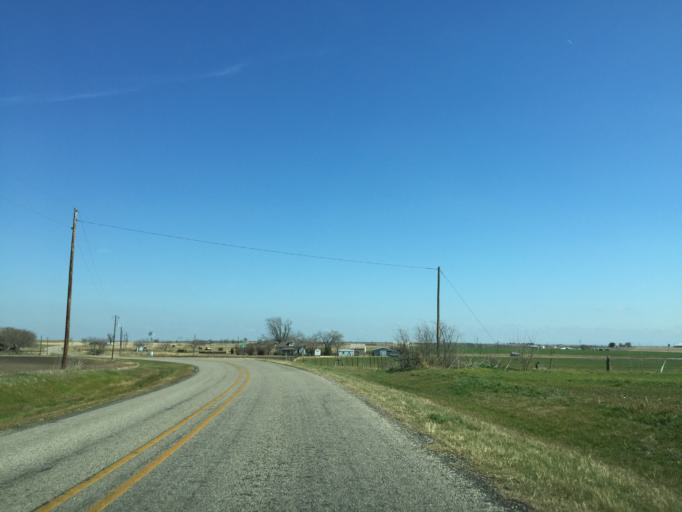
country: US
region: Texas
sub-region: Williamson County
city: Granger
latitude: 30.7474
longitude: -97.5589
